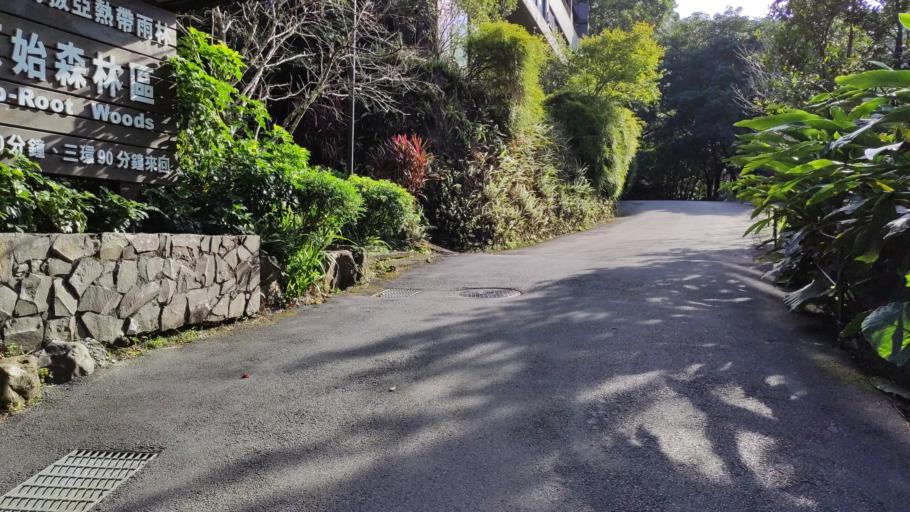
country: TW
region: Taiwan
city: Daxi
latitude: 24.8725
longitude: 121.4076
